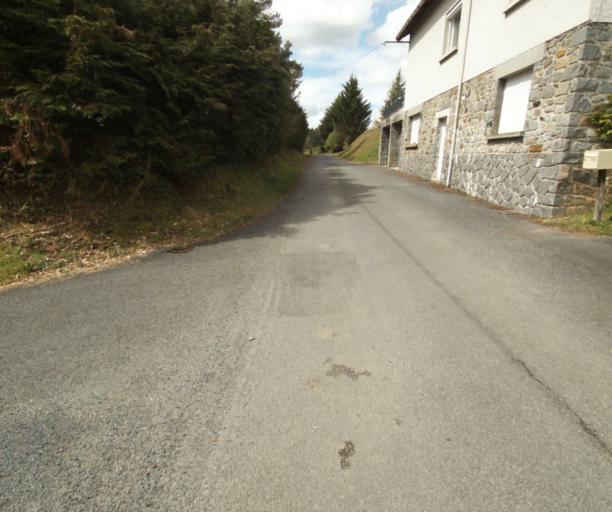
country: FR
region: Limousin
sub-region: Departement de la Correze
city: Sainte-Fortunade
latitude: 45.2002
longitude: 1.8275
